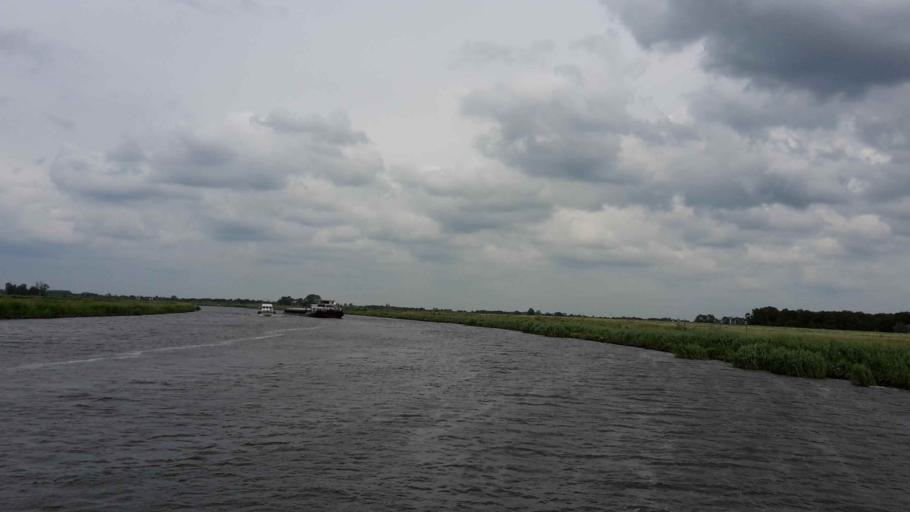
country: NL
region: Friesland
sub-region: Gemeente Boarnsterhim
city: Grou
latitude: 53.1130
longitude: 5.8723
